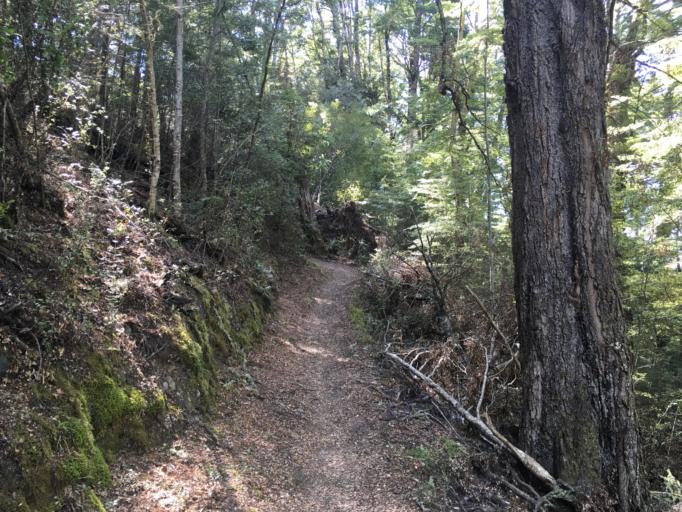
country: NZ
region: Southland
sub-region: Southland District
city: Te Anau
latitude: -45.4858
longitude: 167.6845
